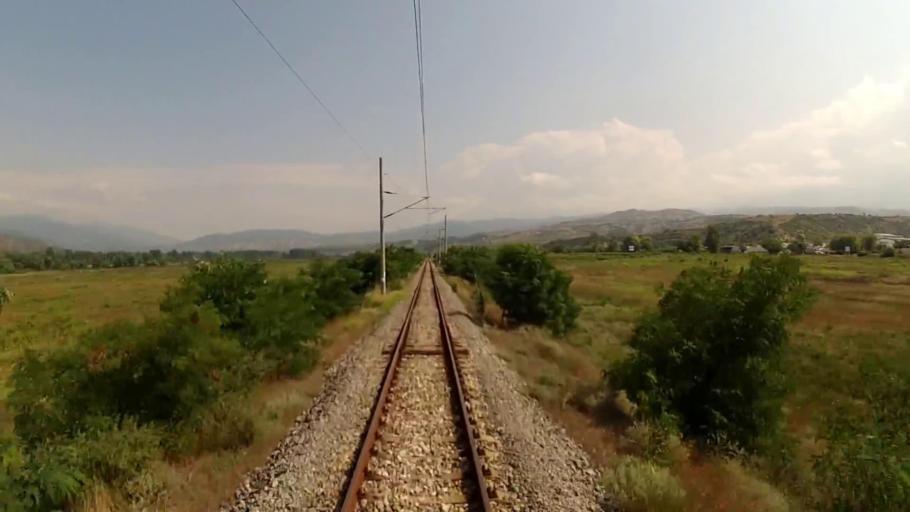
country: BG
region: Blagoevgrad
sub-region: Obshtina Strumyani
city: Strumyani
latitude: 41.6512
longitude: 23.1899
